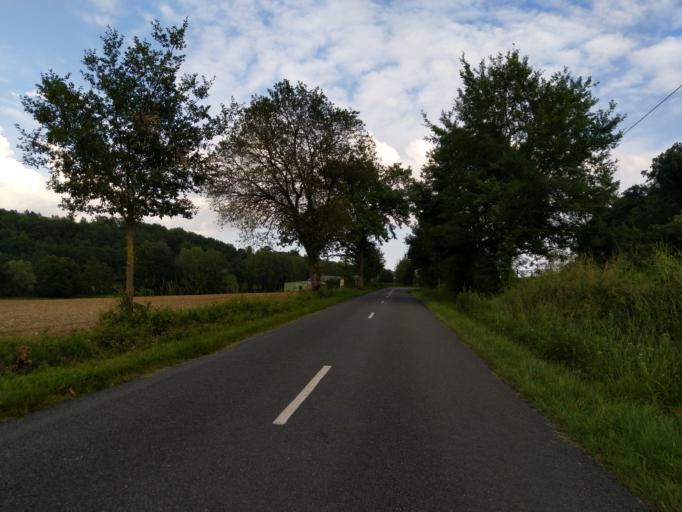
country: FR
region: Midi-Pyrenees
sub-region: Departement du Tarn
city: Realmont
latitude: 43.7979
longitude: 2.1610
